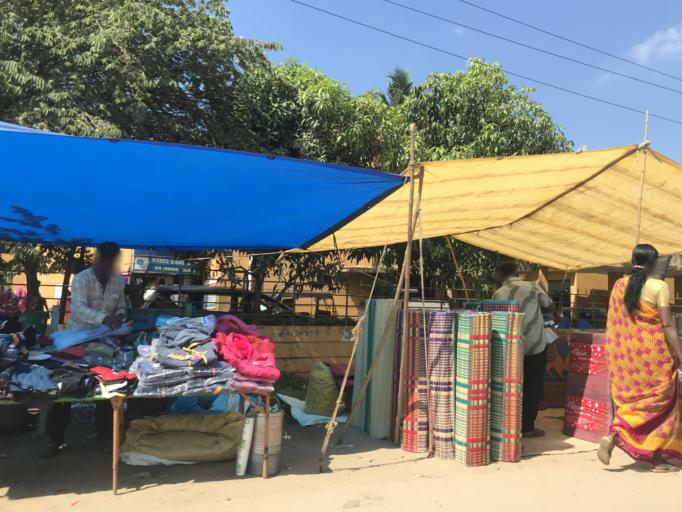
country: IN
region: Karnataka
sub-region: Mysore
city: Heggadadevankote
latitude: 12.0884
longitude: 76.3317
